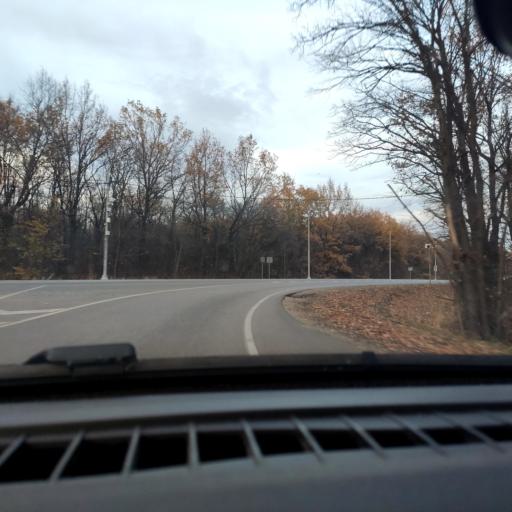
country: RU
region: Voronezj
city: Devitsa
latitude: 51.6330
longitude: 38.9933
